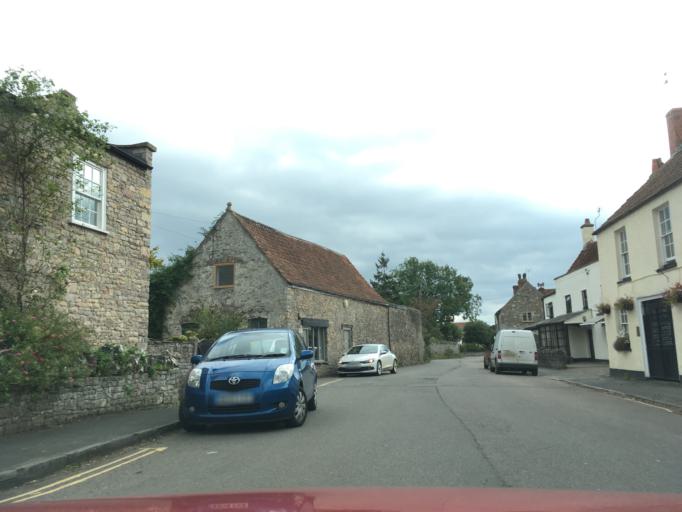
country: GB
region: England
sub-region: South Gloucestershire
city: Almondsbury
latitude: 51.5827
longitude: -2.5770
